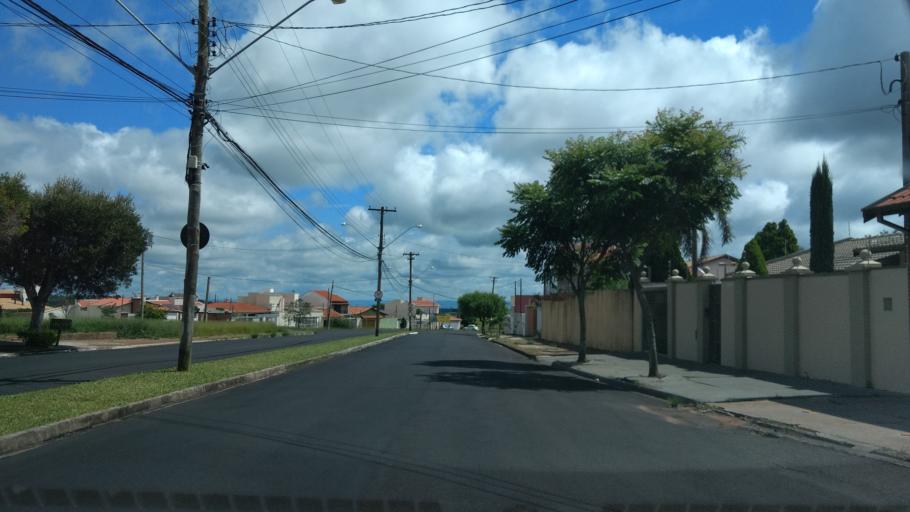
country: BR
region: Sao Paulo
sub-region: Botucatu
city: Botucatu
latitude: -22.8543
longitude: -48.4400
